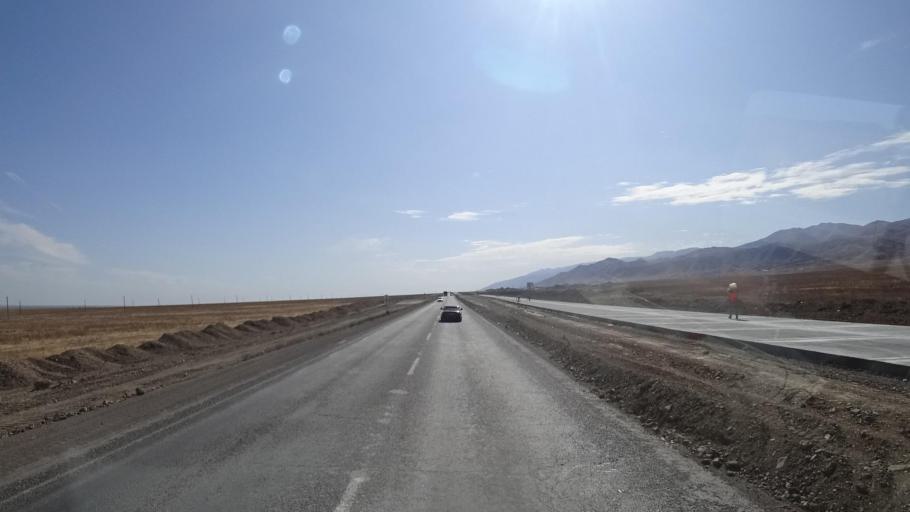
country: KG
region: Chuy
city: Ivanovka
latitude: 43.3961
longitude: 75.1263
